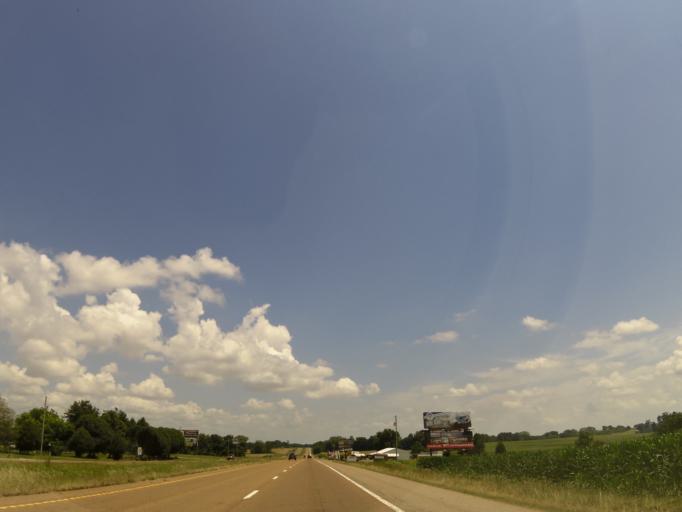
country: US
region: Tennessee
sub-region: Lauderdale County
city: Halls
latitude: 35.9482
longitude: -89.3092
